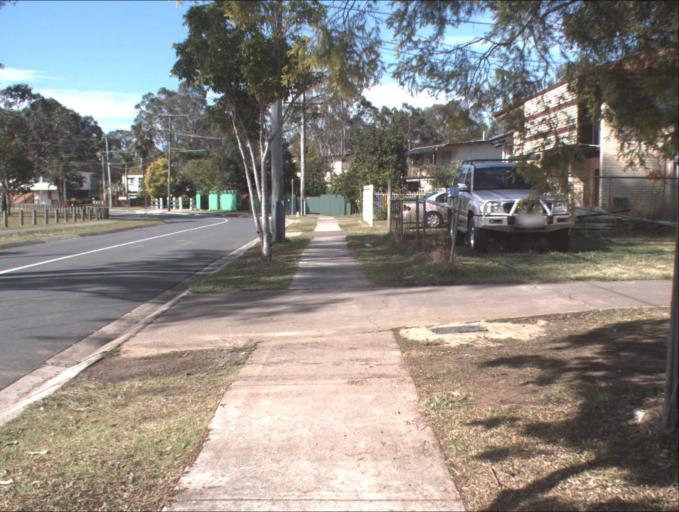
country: AU
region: Queensland
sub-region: Logan
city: Slacks Creek
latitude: -27.6453
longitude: 153.1339
